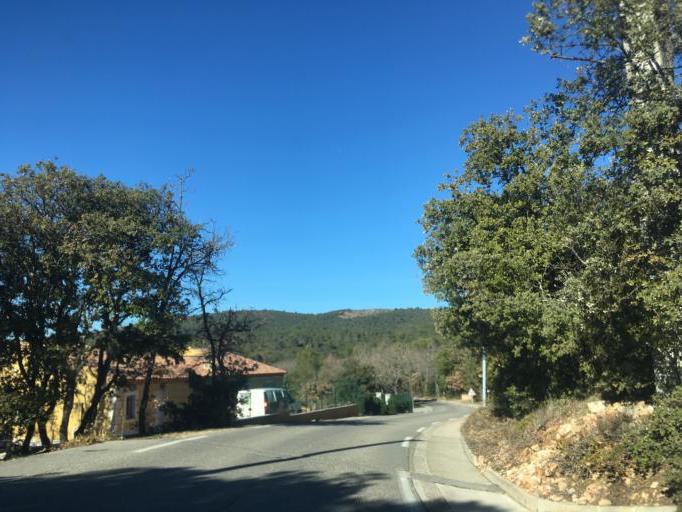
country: FR
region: Provence-Alpes-Cote d'Azur
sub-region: Departement du Var
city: Barjols
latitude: 43.5933
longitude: 6.0340
